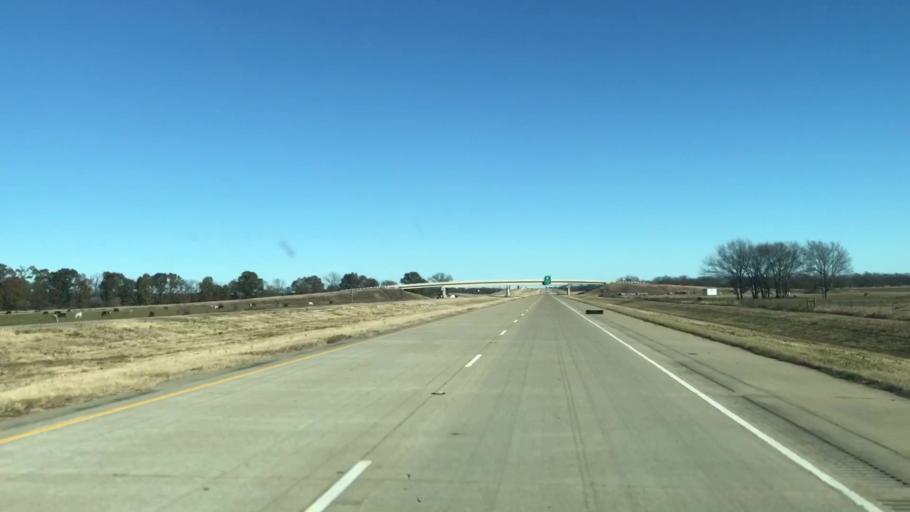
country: US
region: Louisiana
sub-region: Caddo Parish
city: Vivian
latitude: 32.8414
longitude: -93.8692
